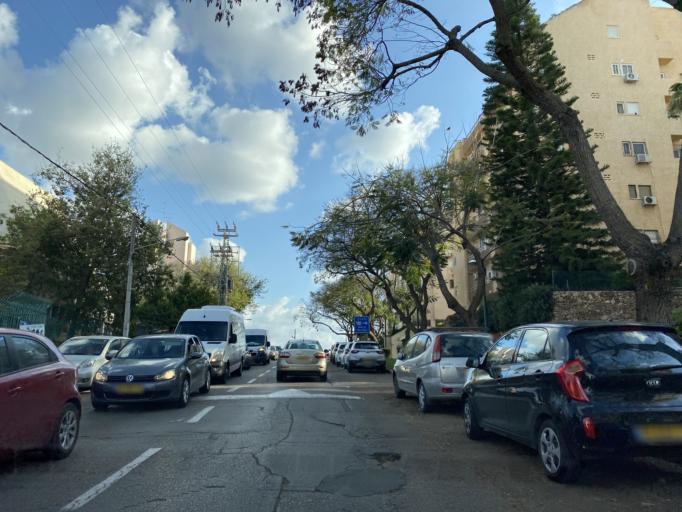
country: IL
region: Central District
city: Kfar Saba
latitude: 32.1707
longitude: 34.9130
